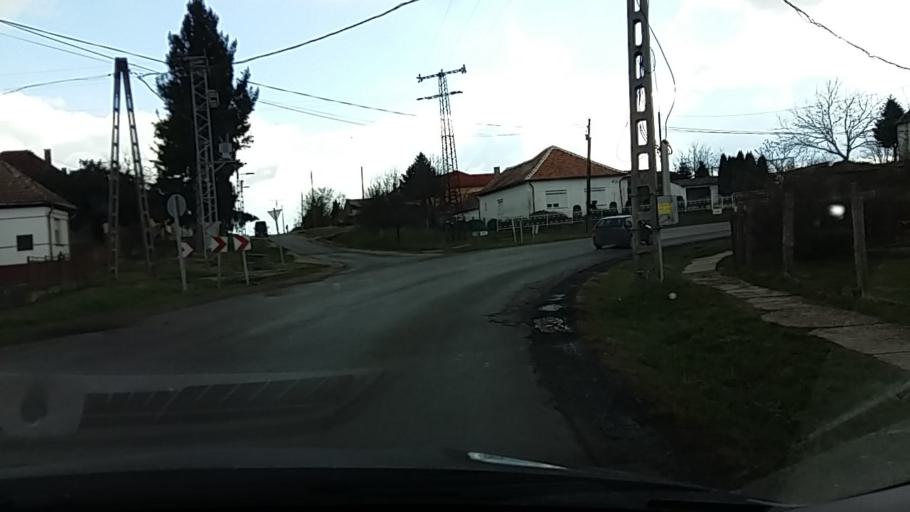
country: HU
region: Somogy
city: Bohonye
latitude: 46.4124
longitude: 17.3860
